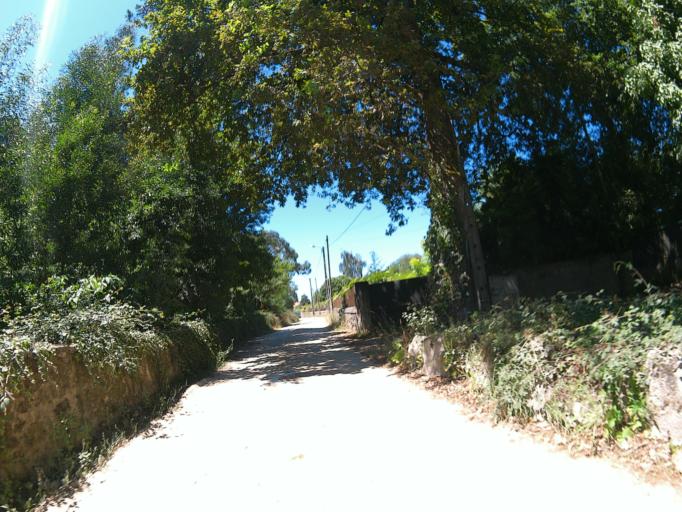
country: PT
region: Viana do Castelo
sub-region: Viana do Castelo
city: Darque
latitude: 41.7024
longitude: -8.7444
